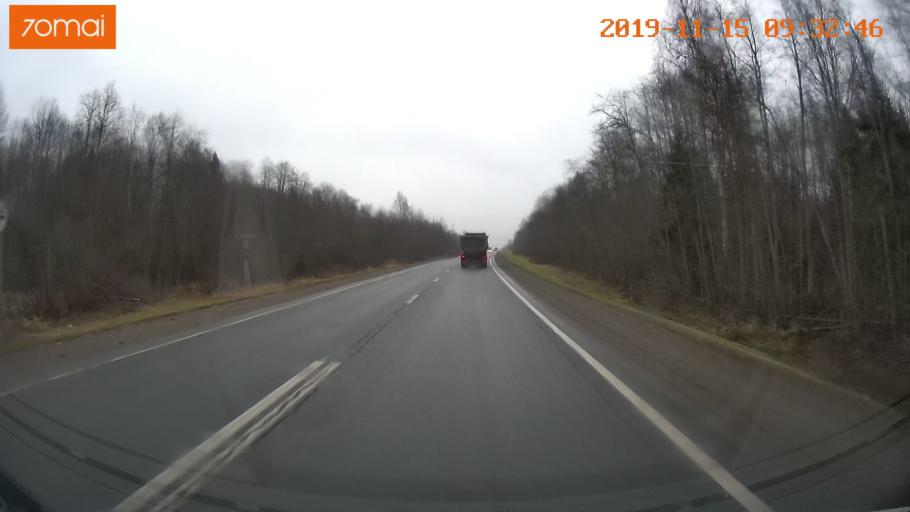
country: RU
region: Vologda
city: Sheksna
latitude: 59.2701
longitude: 38.3432
